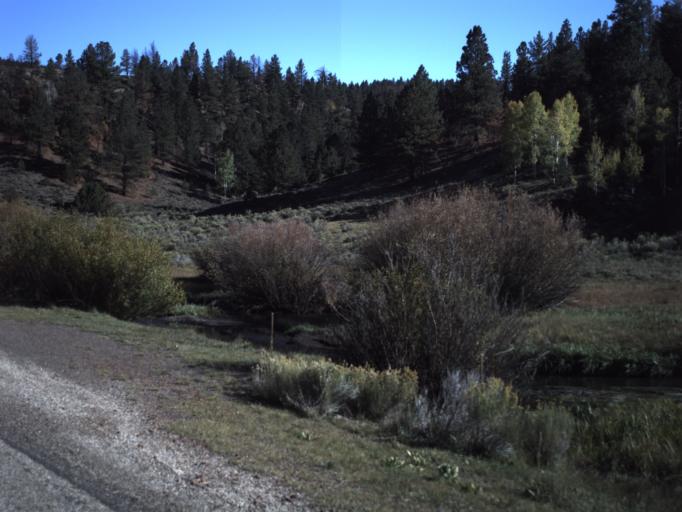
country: US
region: Utah
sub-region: Garfield County
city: Panguitch
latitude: 37.7364
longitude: -112.6002
